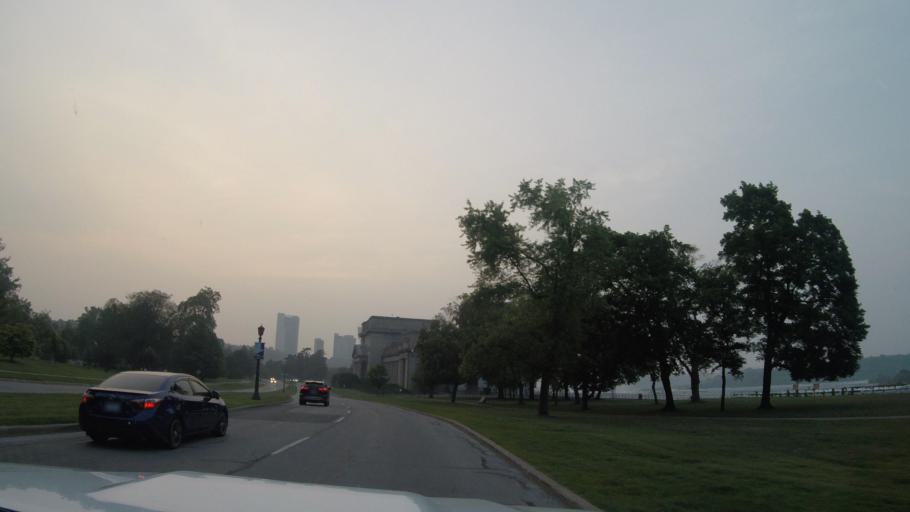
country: US
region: New York
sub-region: Niagara County
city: Niagara Falls
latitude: 43.0704
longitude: -79.0724
